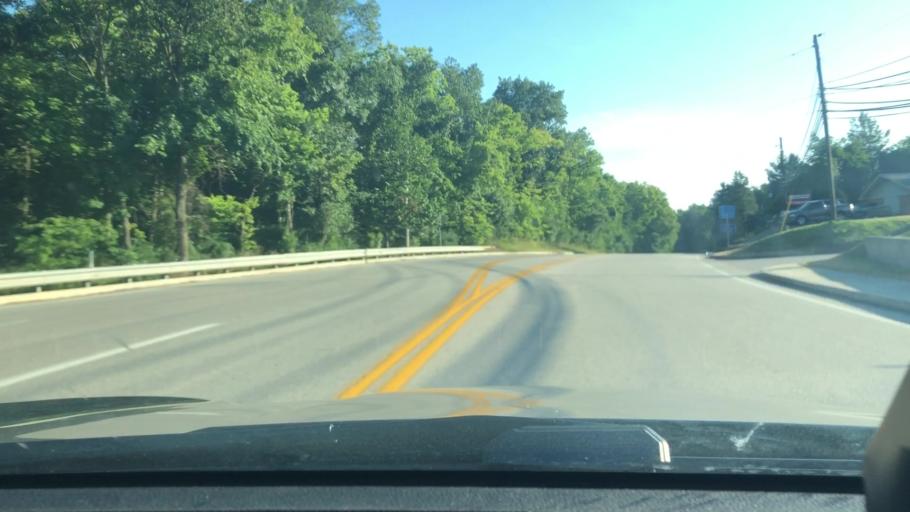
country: US
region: Pennsylvania
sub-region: Cumberland County
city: Mechanicsburg
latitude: 40.2456
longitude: -77.0059
